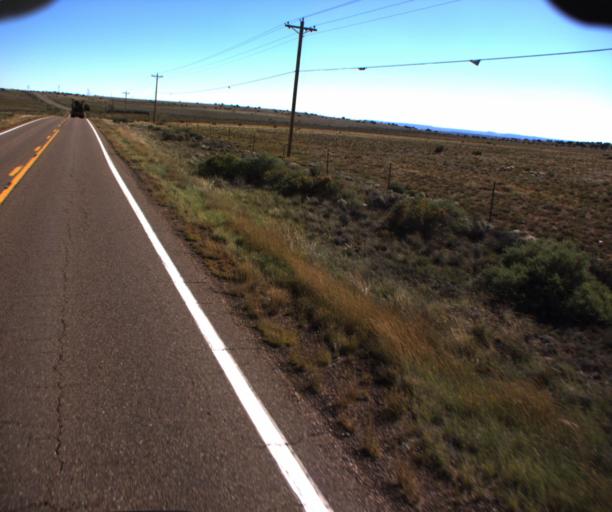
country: US
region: Arizona
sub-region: Apache County
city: Saint Johns
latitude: 34.4899
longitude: -109.5223
